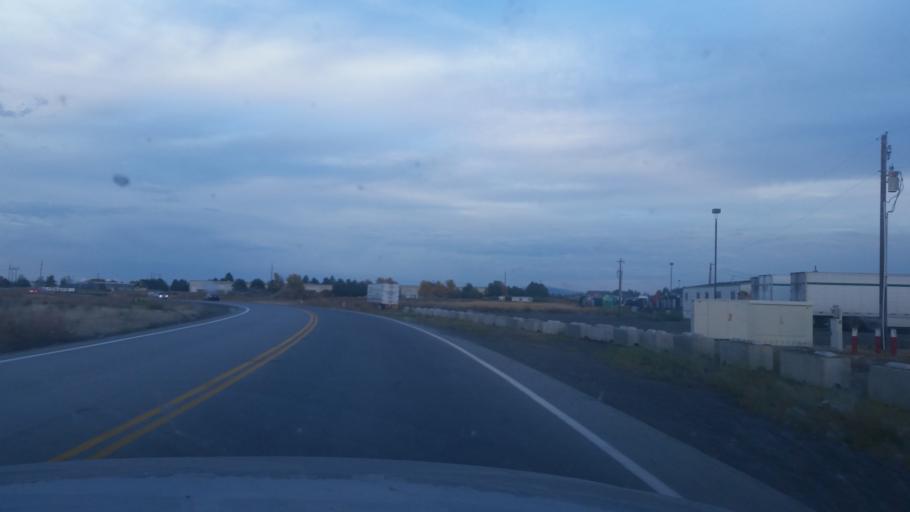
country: US
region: Washington
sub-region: Spokane County
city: Airway Heights
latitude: 47.5875
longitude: -117.5635
